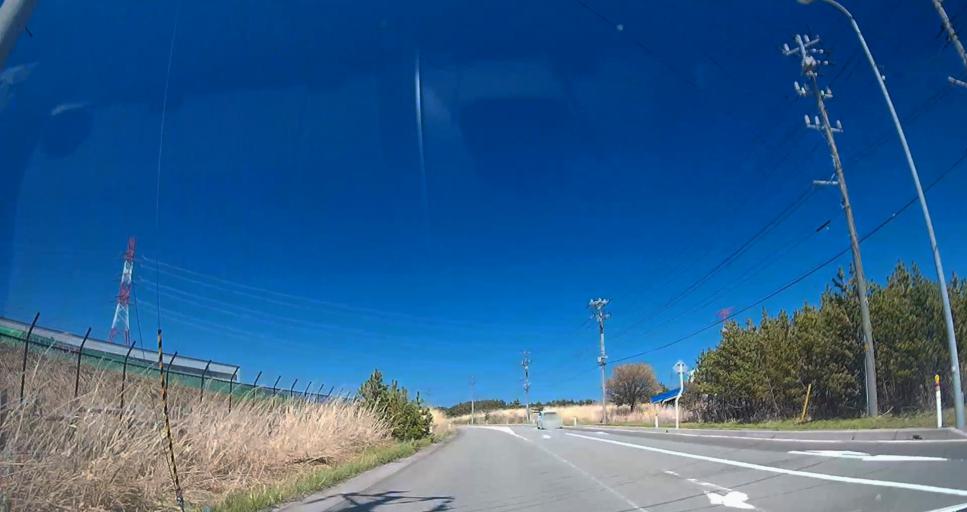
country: JP
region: Hokkaido
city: Hakodate
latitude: 41.5090
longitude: 140.9185
